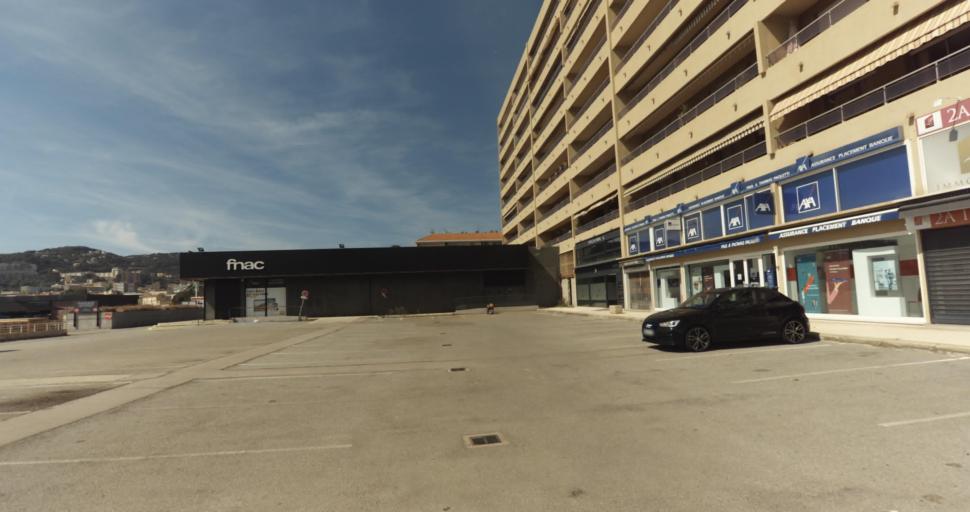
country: FR
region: Corsica
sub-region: Departement de la Corse-du-Sud
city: Ajaccio
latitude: 41.9316
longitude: 8.7476
